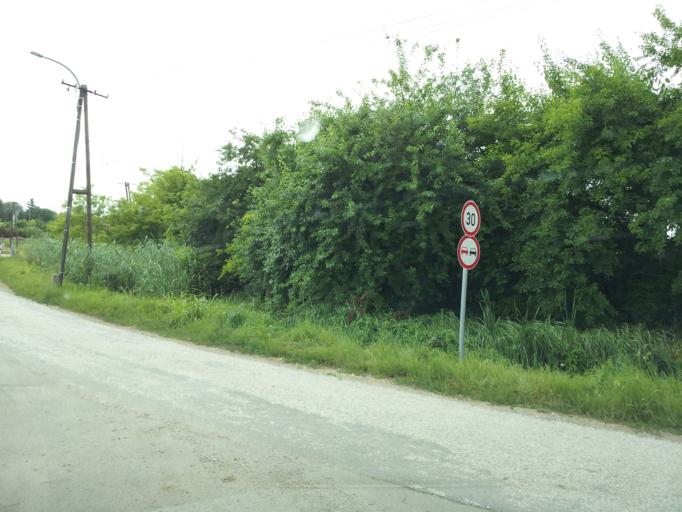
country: HU
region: Fejer
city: Enying
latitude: 46.9248
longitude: 18.2400
